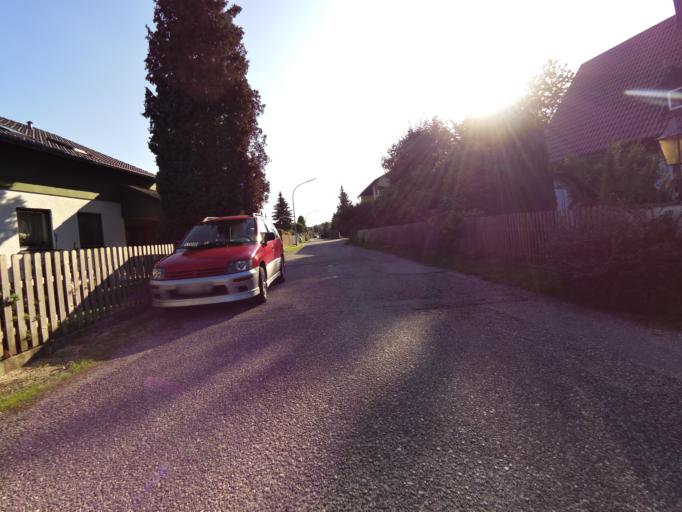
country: DE
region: Bavaria
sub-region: Lower Bavaria
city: Stallwang
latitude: 48.5684
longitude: 12.2022
